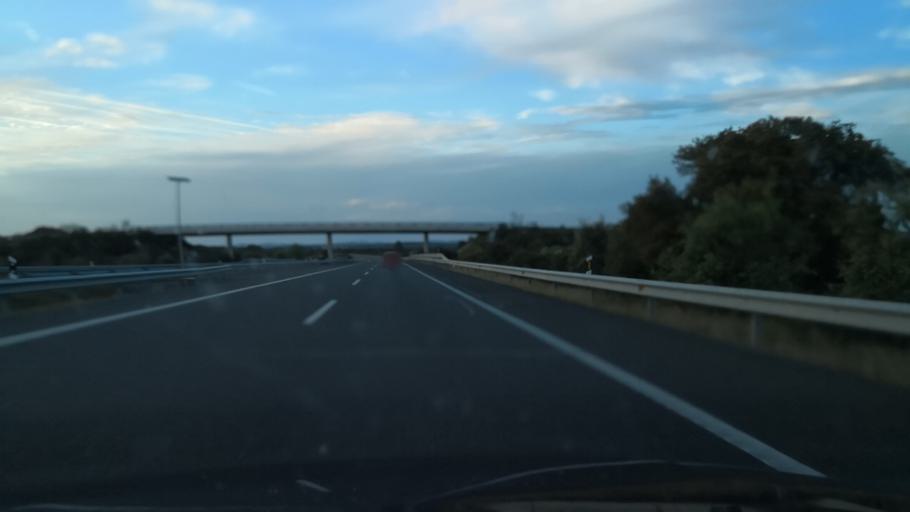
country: ES
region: Extremadura
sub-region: Provincia de Caceres
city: Alcuescar
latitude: 39.1888
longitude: -6.2767
